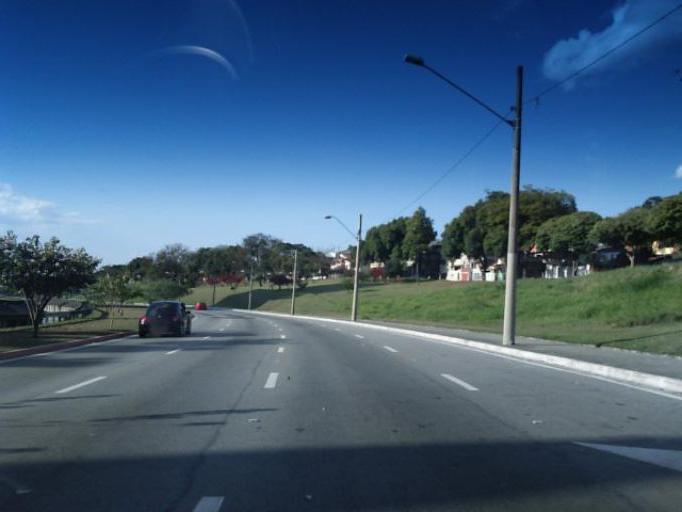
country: BR
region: Sao Paulo
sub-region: Sao Jose Dos Campos
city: Sao Jose dos Campos
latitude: -23.1863
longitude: -45.8779
